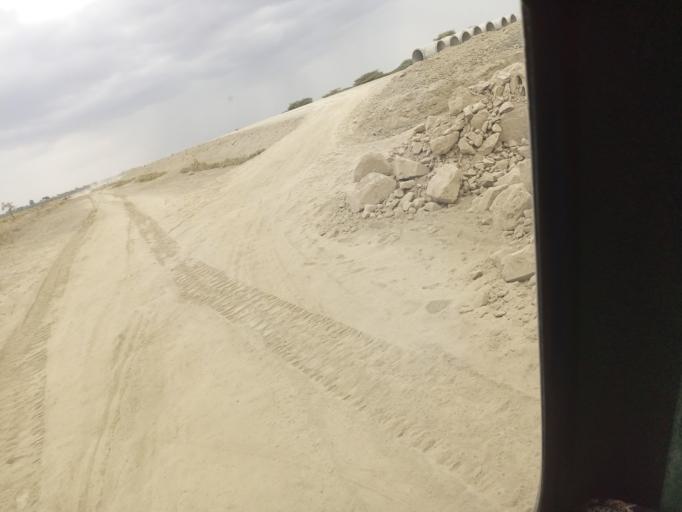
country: ET
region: Oromiya
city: Ziway
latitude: 7.8644
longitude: 38.6707
